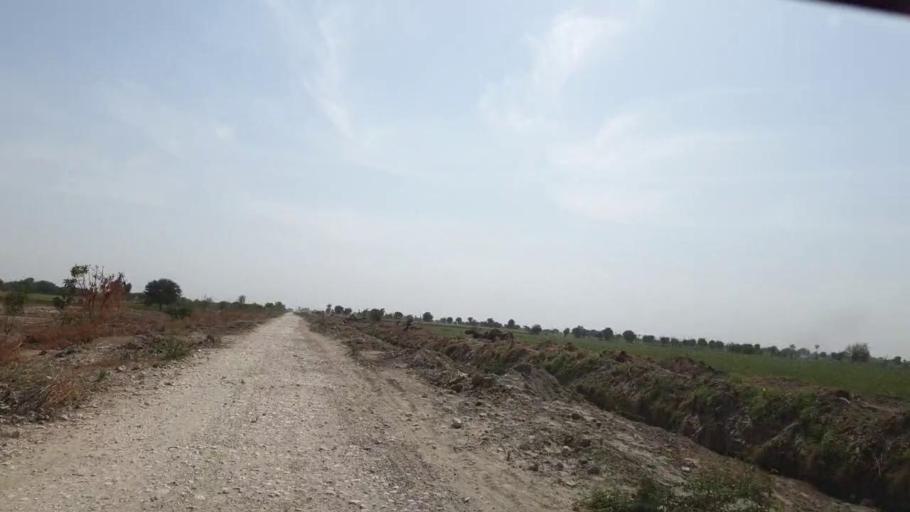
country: PK
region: Sindh
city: Nabisar
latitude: 25.0950
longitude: 69.5817
